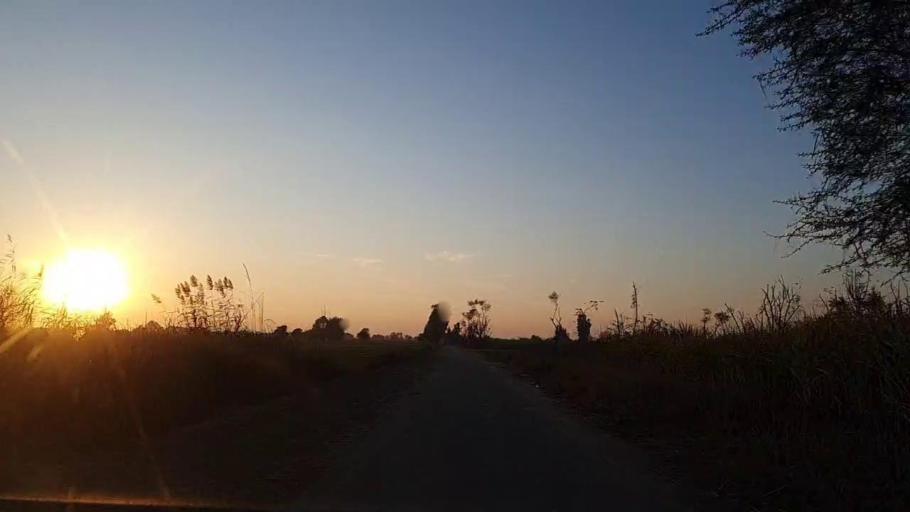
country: PK
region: Sindh
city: Bandhi
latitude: 26.6203
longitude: 68.3572
